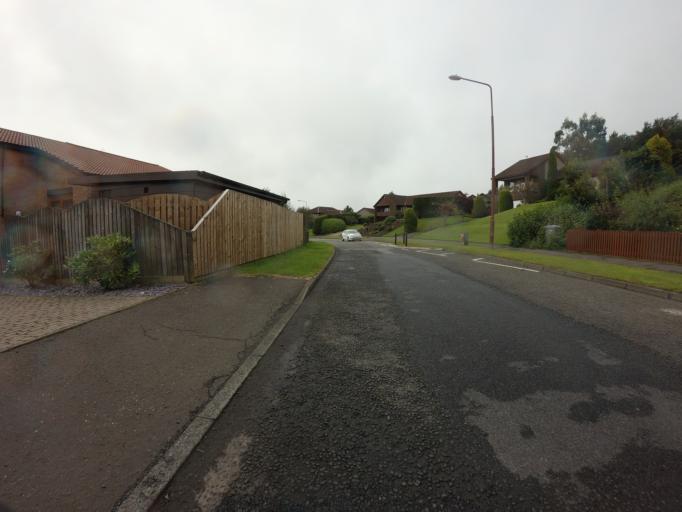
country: GB
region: Scotland
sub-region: West Lothian
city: Livingston
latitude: 55.9099
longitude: -3.5423
